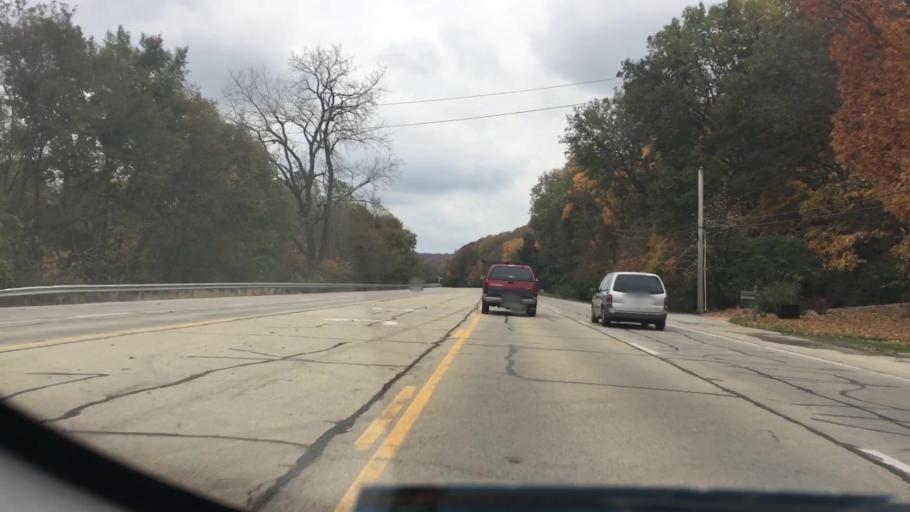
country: US
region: Illinois
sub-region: Peoria County
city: Peoria Heights
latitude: 40.7830
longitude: -89.5774
